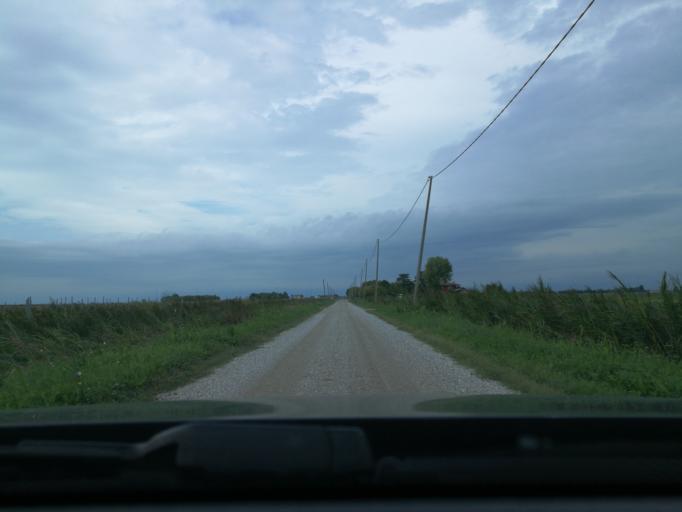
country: IT
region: Friuli Venezia Giulia
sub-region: Provincia di Udine
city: Pertegada
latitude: 45.7200
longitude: 13.0694
